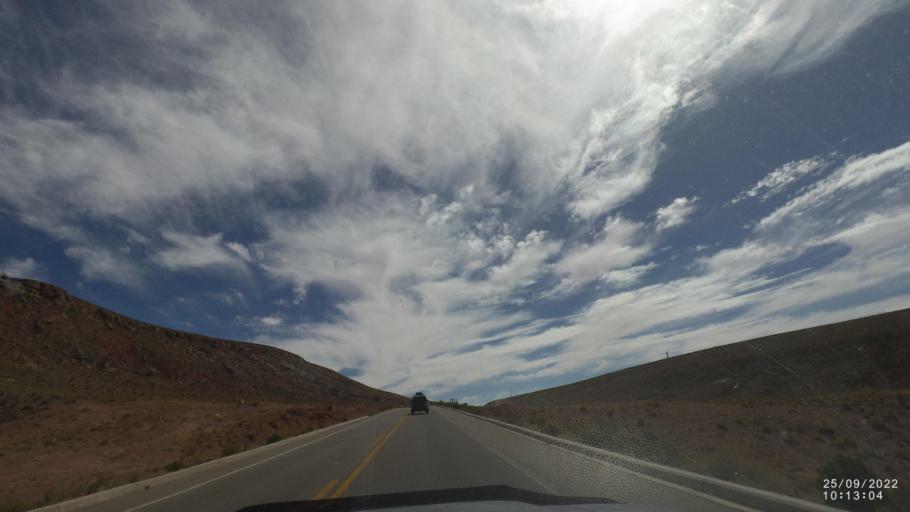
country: BO
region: Potosi
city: Colchani
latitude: -20.0777
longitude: -66.8896
